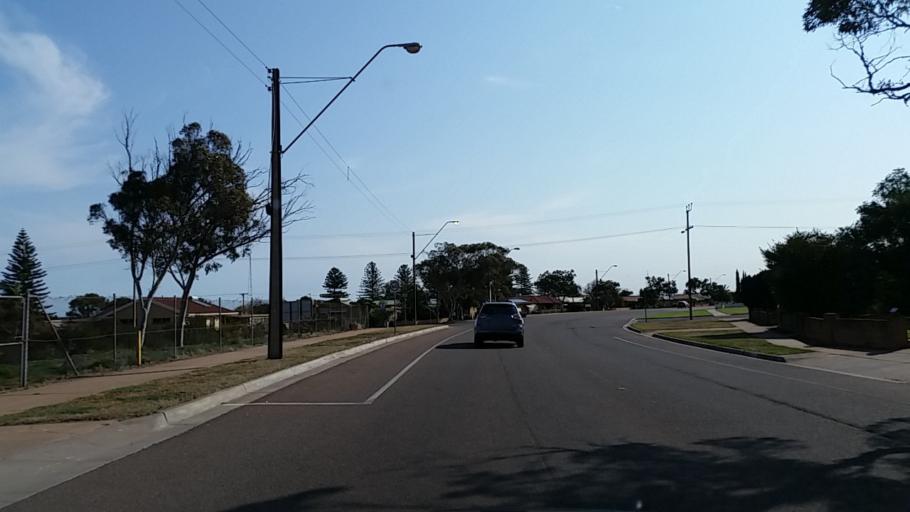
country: AU
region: South Australia
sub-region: Whyalla
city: Whyalla
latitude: -33.0411
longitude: 137.5772
